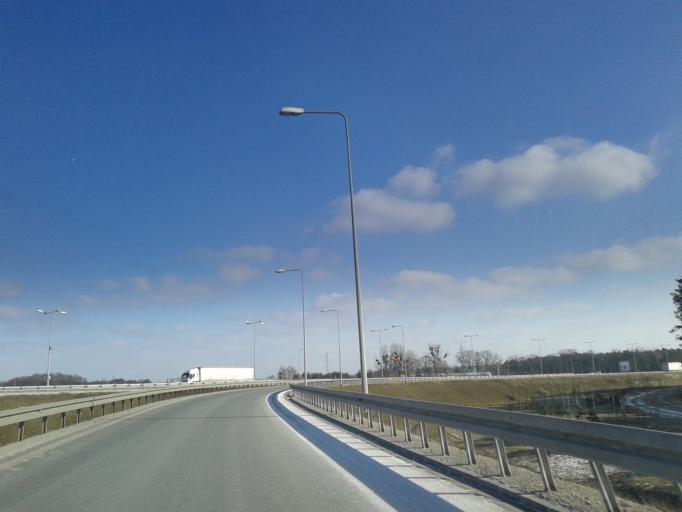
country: PL
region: Kujawsko-Pomorskie
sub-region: Powiat aleksandrowski
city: Ciechocinek
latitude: 52.8655
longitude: 18.7593
